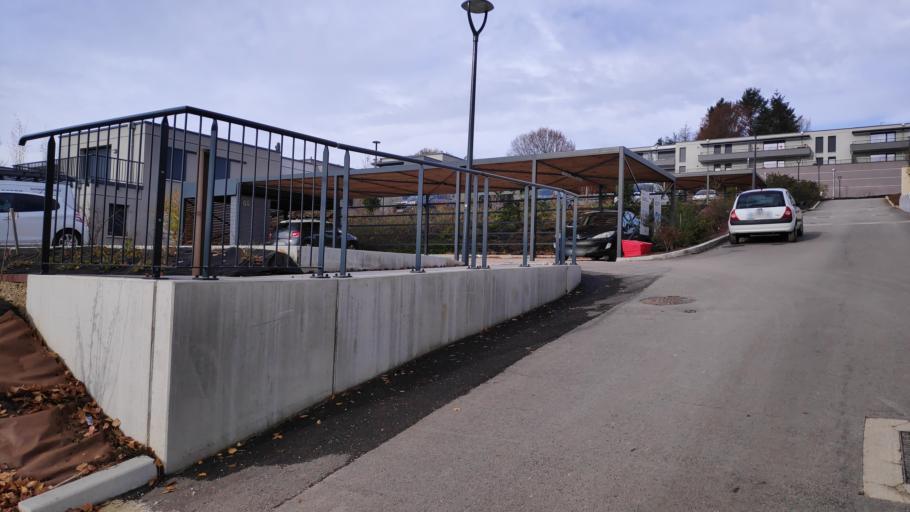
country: FR
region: Franche-Comte
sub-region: Departement du Doubs
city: Pirey
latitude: 47.2342
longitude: 5.9709
